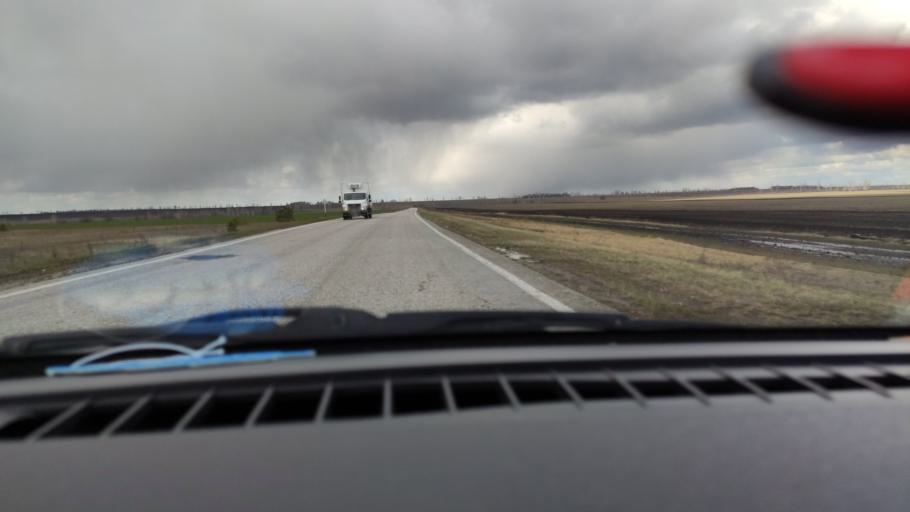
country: RU
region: Samara
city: Povolzhskiy
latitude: 53.7938
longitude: 49.7329
